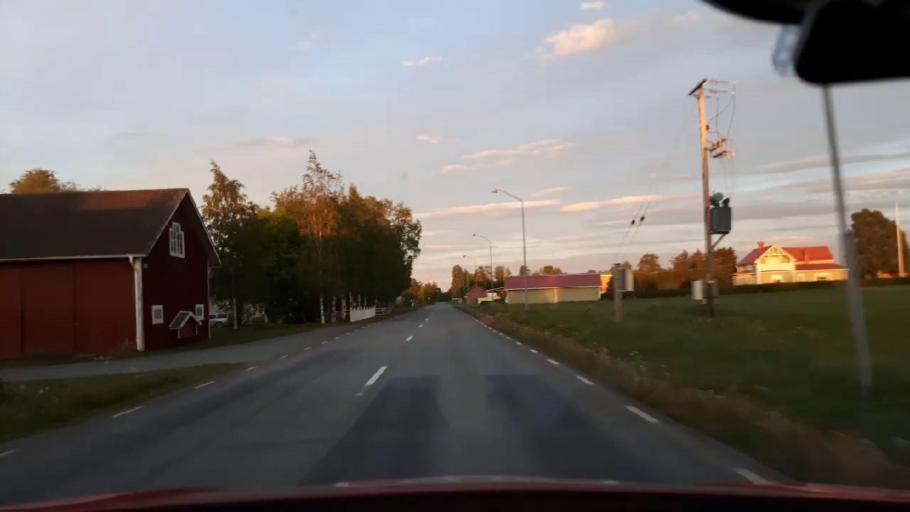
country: SE
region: Jaemtland
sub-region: OEstersunds Kommun
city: Ostersund
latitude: 63.1182
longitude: 14.7198
